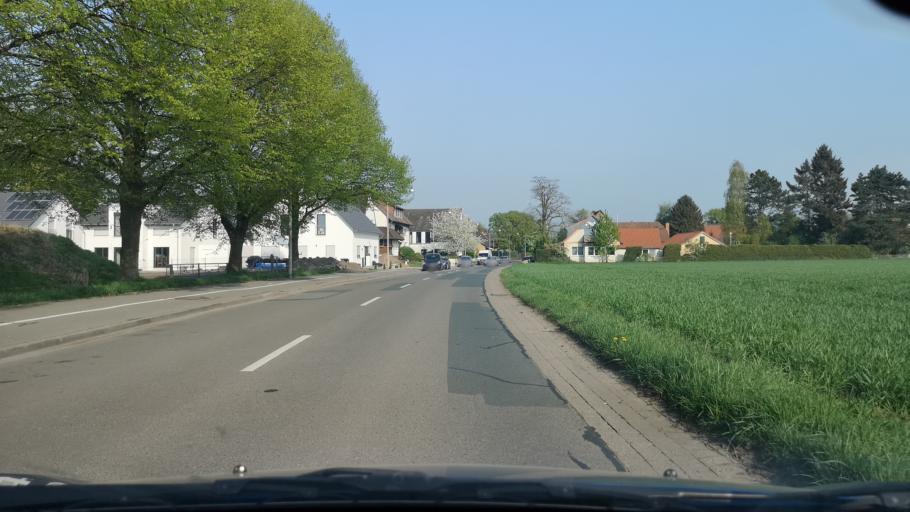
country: DE
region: Lower Saxony
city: Langenhagen
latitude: 52.4473
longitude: 9.6724
